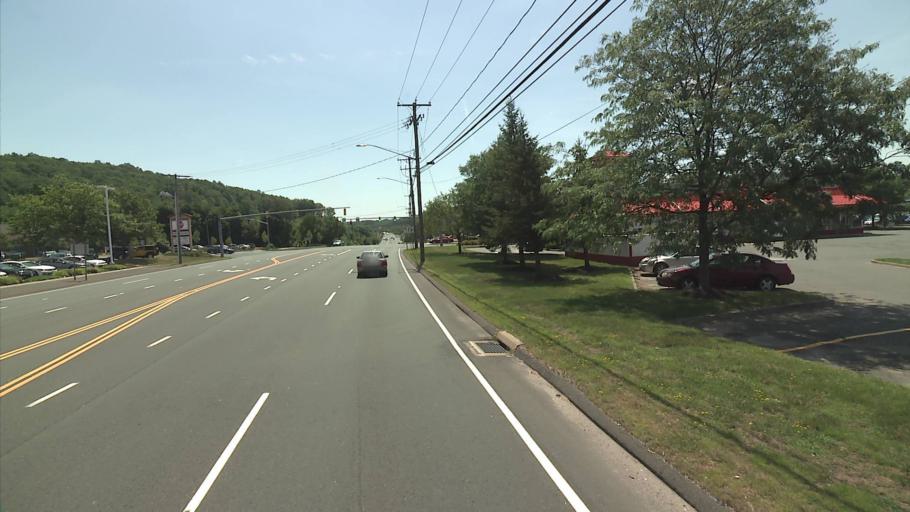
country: US
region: Connecticut
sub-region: Hartford County
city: Plainville
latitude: 41.6764
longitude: -72.8415
